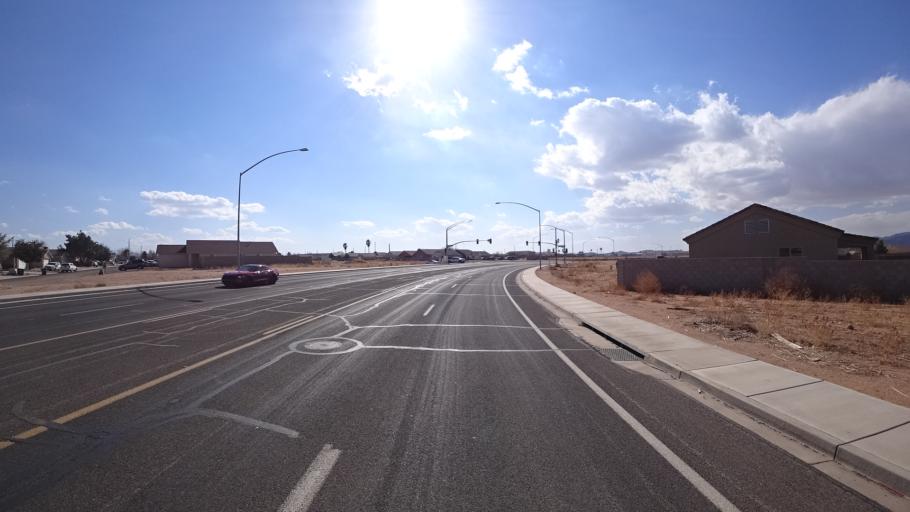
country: US
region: Arizona
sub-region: Mohave County
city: New Kingman-Butler
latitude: 35.2232
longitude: -113.9979
